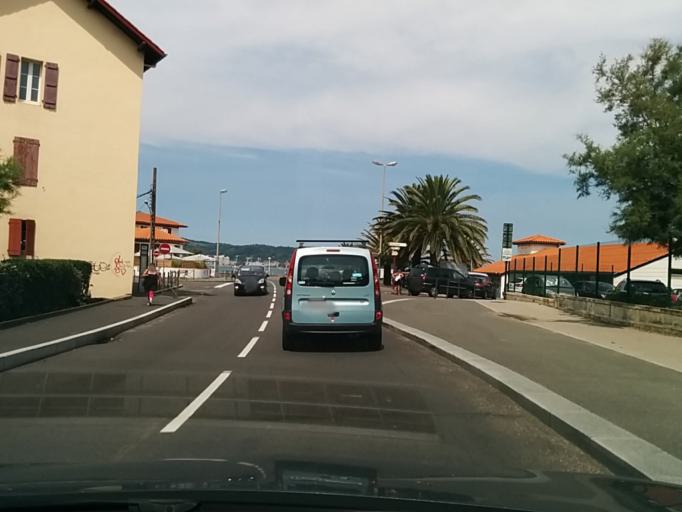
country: FR
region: Aquitaine
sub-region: Departement des Pyrenees-Atlantiques
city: Hendaye
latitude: 43.3754
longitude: -1.7615
